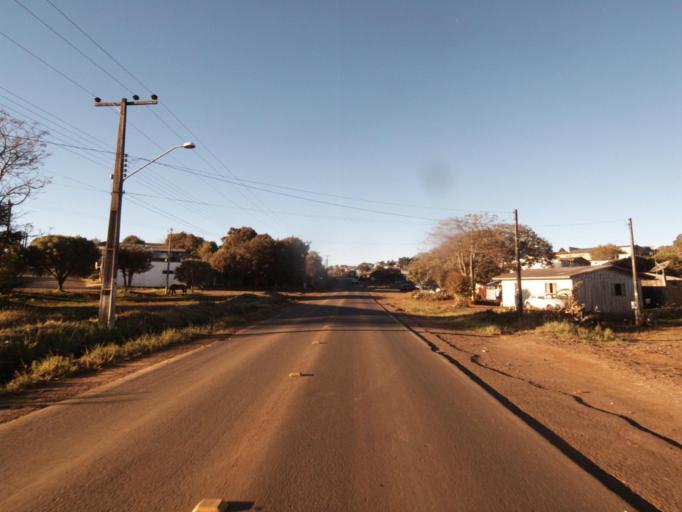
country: AR
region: Misiones
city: Bernardo de Irigoyen
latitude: -26.2619
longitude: -53.6212
